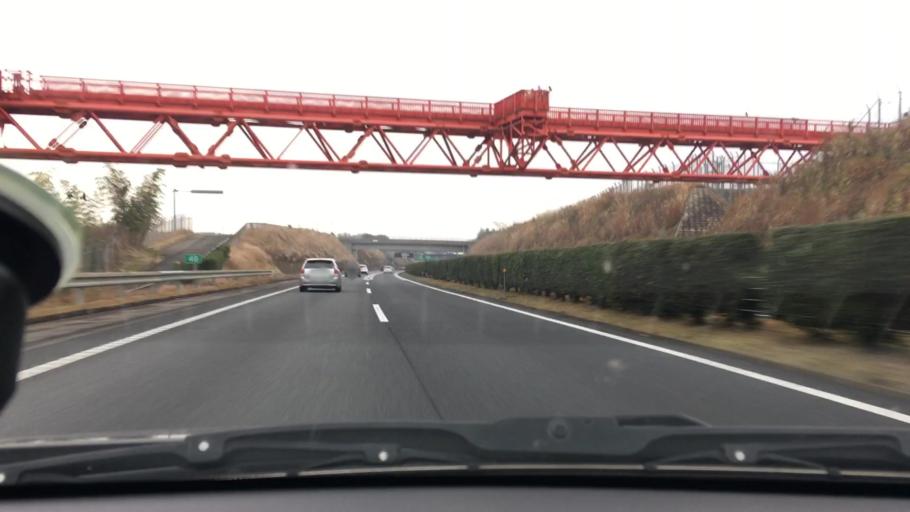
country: JP
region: Chiba
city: Narita
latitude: 35.8080
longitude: 140.3757
